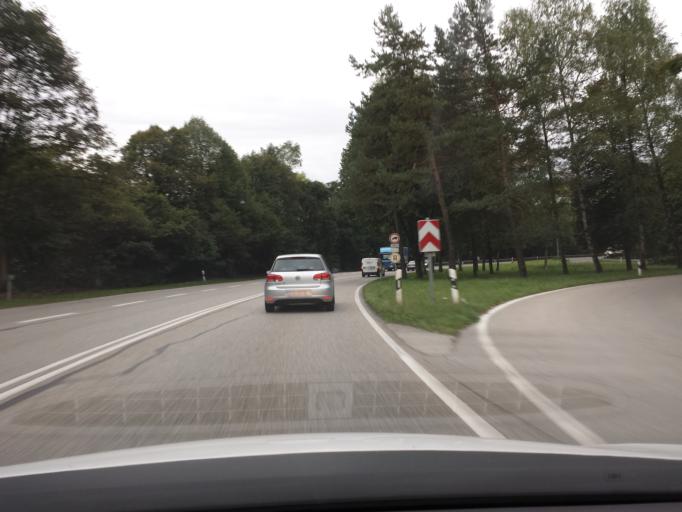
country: DE
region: Bavaria
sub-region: Upper Bavaria
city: Bad Reichenhall
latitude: 47.7401
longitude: 12.8959
